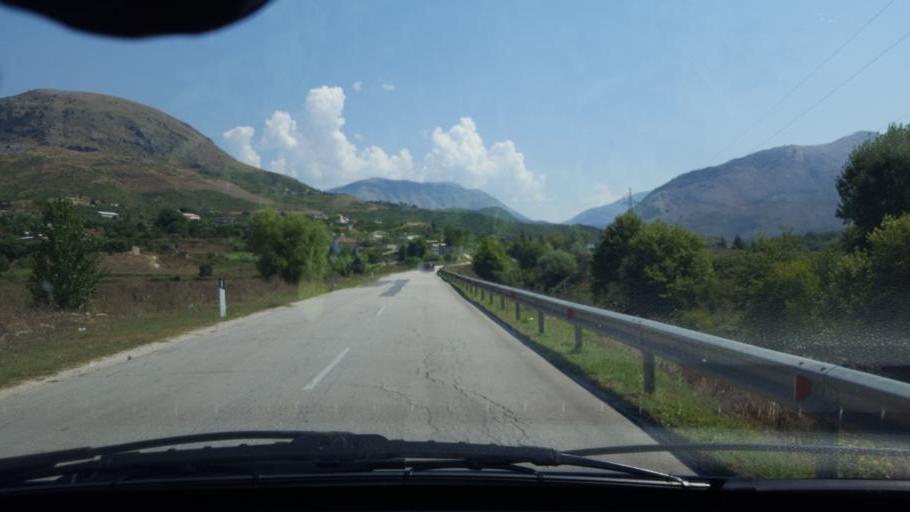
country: AL
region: Vlore
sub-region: Rrethi i Delvines
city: Mesopotam
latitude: 39.9101
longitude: 20.0985
